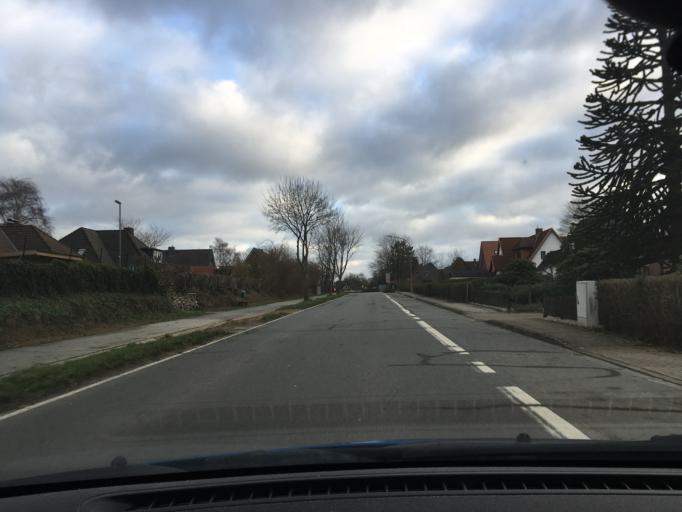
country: DE
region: Schleswig-Holstein
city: Schenefeld
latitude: 54.0481
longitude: 9.4739
